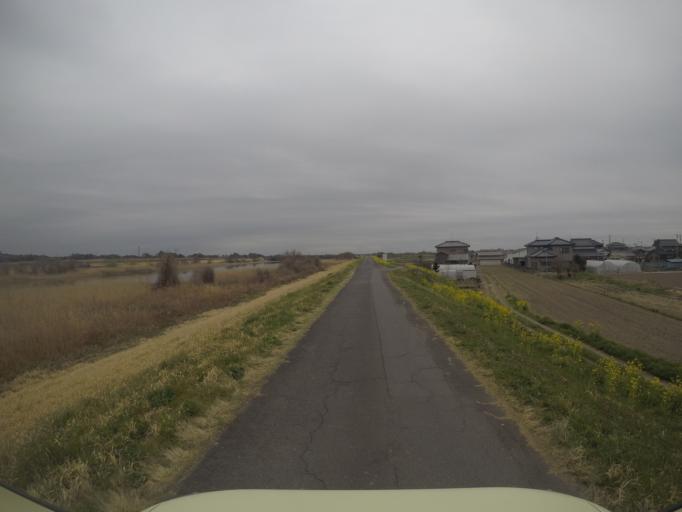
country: JP
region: Ibaraki
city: Ishige
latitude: 36.0762
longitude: 140.0044
